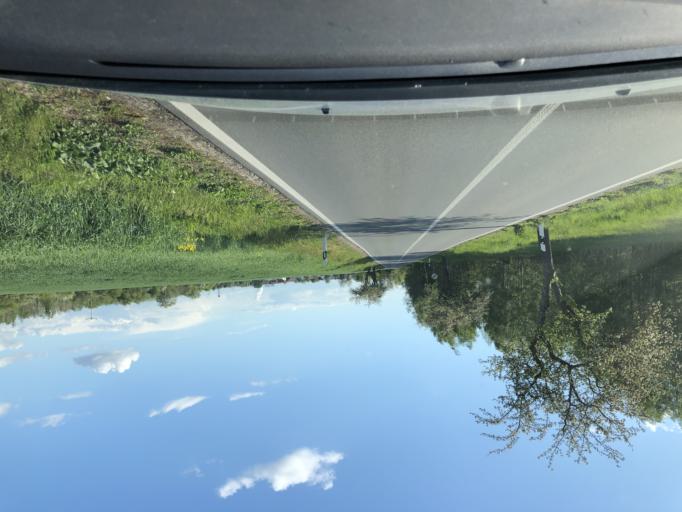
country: DE
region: Saxony
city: Regis-Breitingen
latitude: 51.0991
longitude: 12.4339
